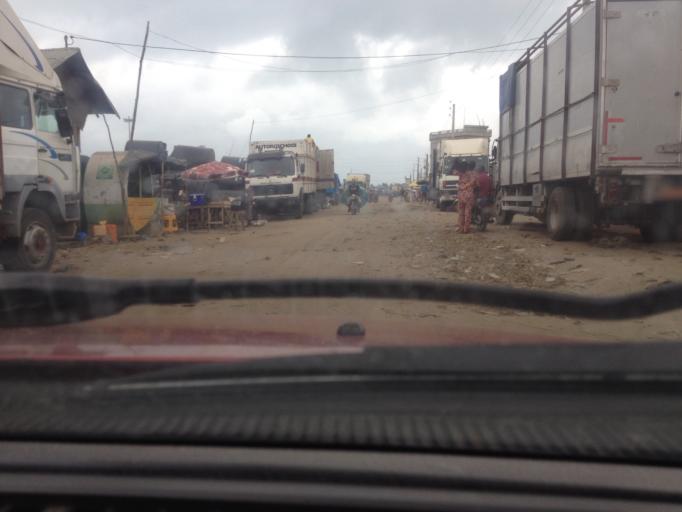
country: BJ
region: Queme
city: Porto-Novo
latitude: 6.3822
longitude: 2.7020
